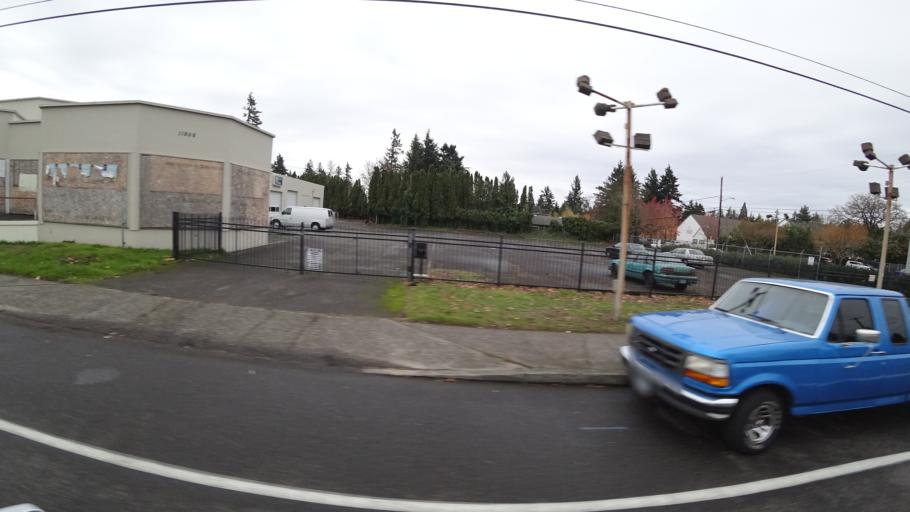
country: US
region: Oregon
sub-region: Multnomah County
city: Lents
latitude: 45.5335
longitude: -122.5409
